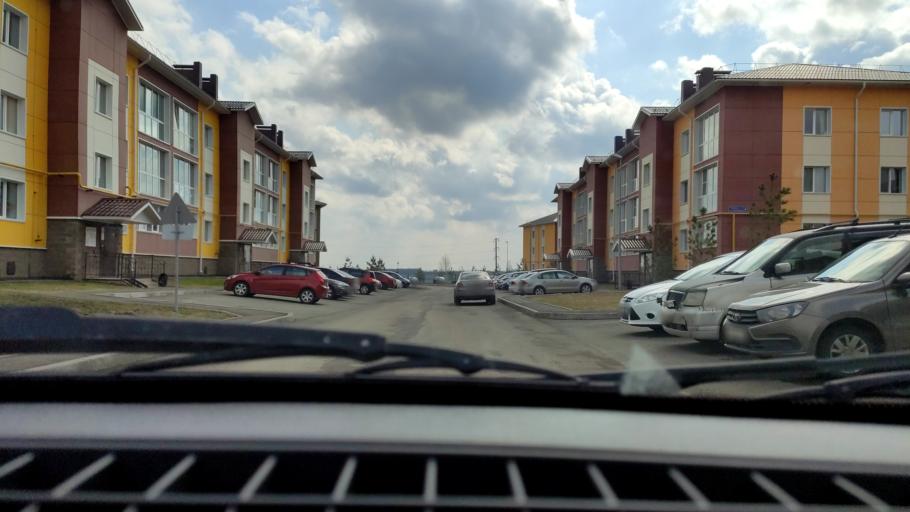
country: RU
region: Bashkortostan
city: Ufa
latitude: 54.5913
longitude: 55.9165
